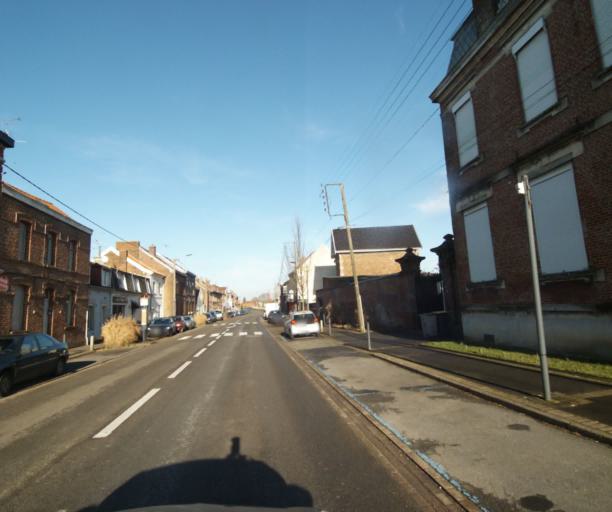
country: FR
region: Nord-Pas-de-Calais
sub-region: Departement du Nord
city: Aulnoy-lez-Valenciennes
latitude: 50.3356
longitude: 3.5241
